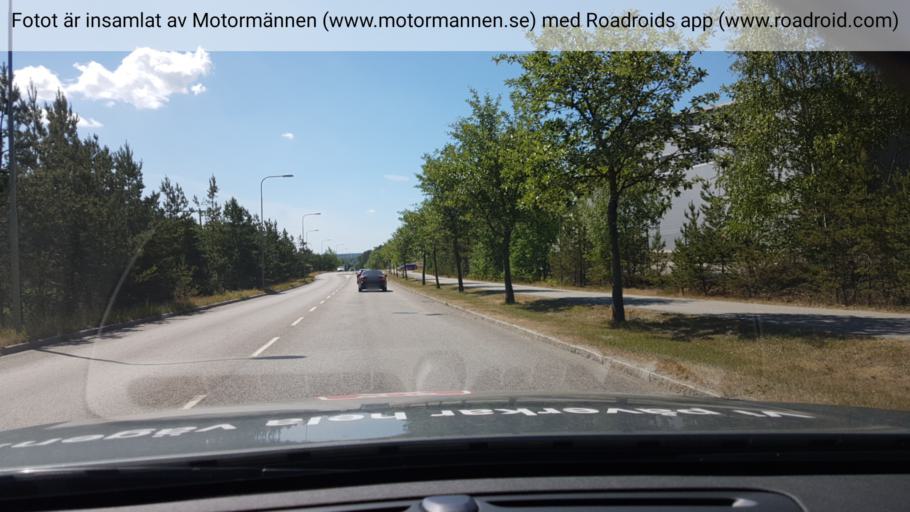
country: SE
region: Stockholm
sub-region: Nacka Kommun
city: Alta
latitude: 59.2412
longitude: 18.1953
